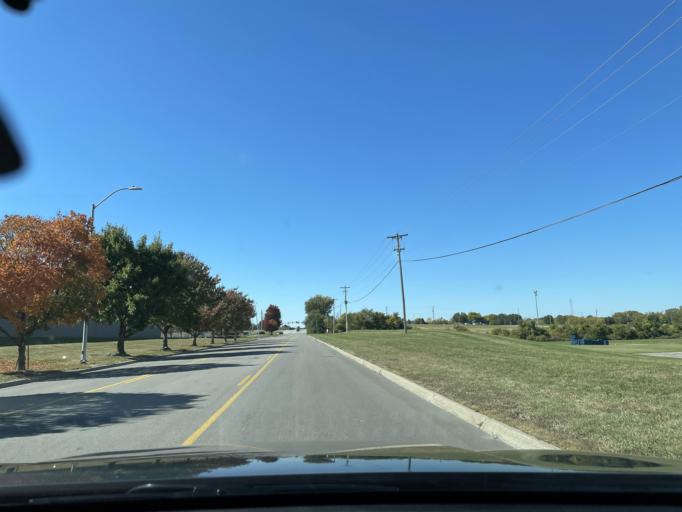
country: US
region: Missouri
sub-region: Buchanan County
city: Saint Joseph
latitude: 39.7555
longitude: -94.7631
